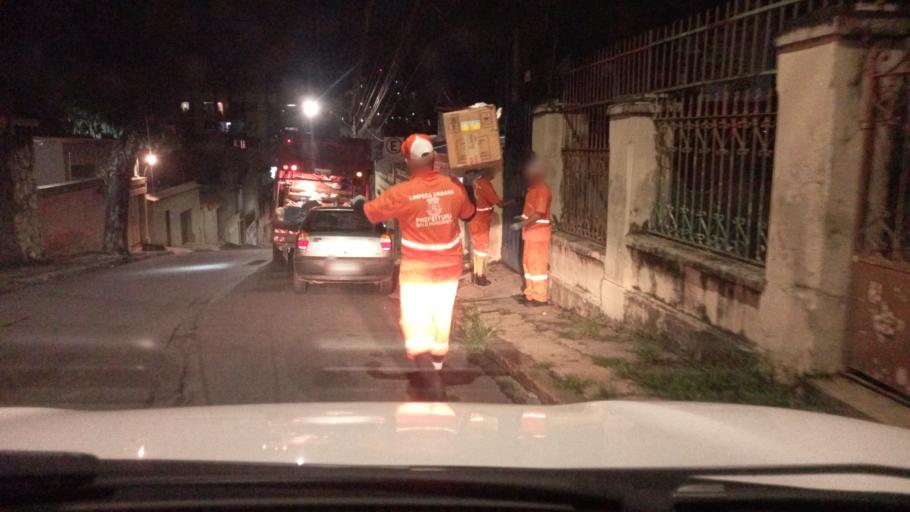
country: BR
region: Minas Gerais
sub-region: Belo Horizonte
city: Belo Horizonte
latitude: -19.9082
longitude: -43.9460
